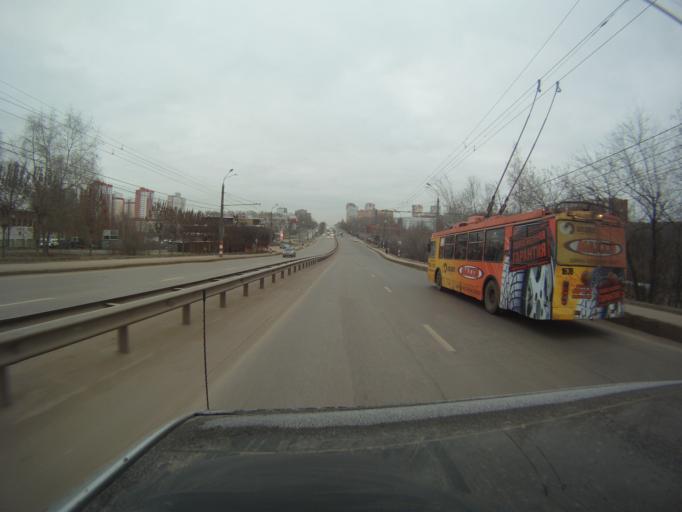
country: RU
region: Nizjnij Novgorod
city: Nizhniy Novgorod
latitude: 56.2900
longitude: 44.0361
